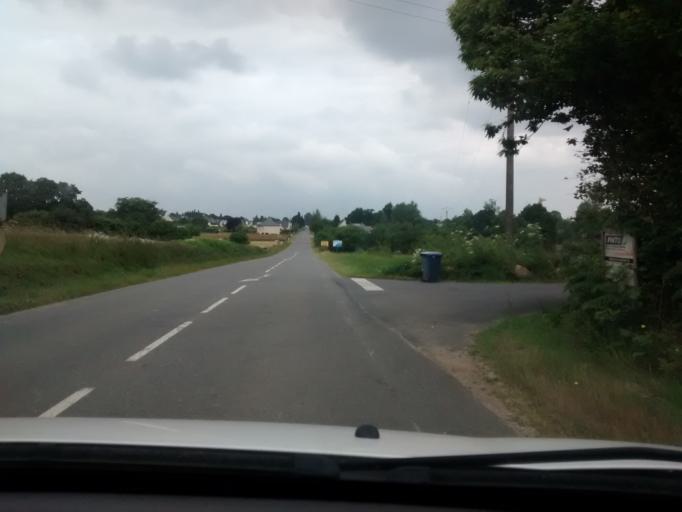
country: FR
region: Brittany
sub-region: Departement d'Ille-et-Vilaine
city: Liffre
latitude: 48.1994
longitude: -1.5106
